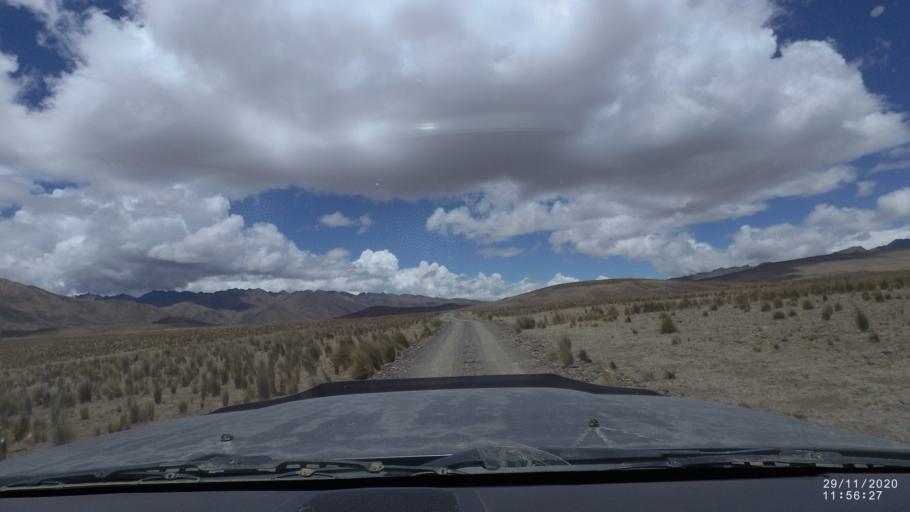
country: BO
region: Cochabamba
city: Cochabamba
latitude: -17.1639
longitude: -66.2709
